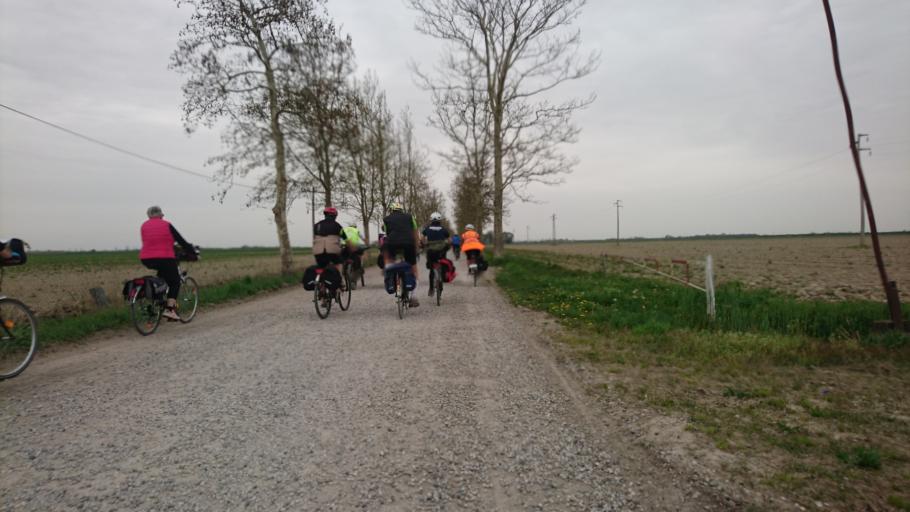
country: IT
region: Veneto
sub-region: Provincia di Venezia
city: Lugugnana
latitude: 45.6749
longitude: 12.9677
